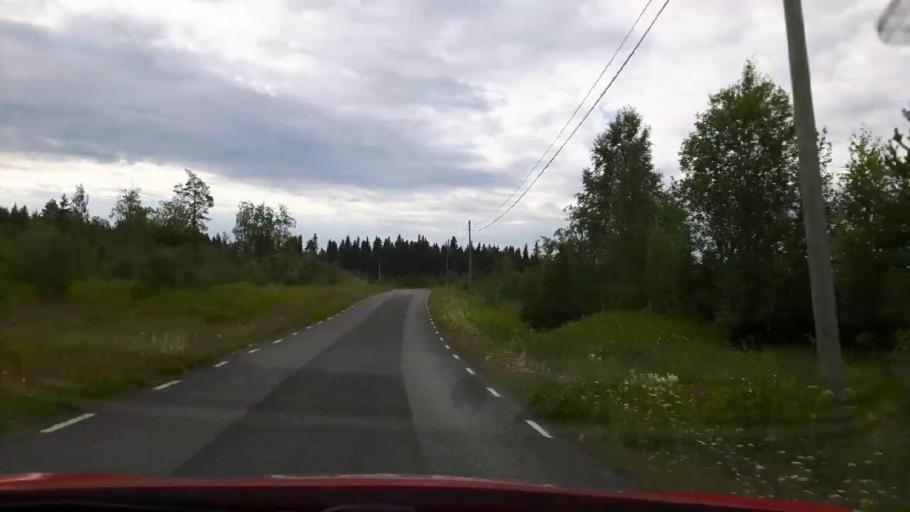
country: SE
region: Jaemtland
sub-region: OEstersunds Kommun
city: Lit
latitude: 63.3927
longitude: 15.0107
